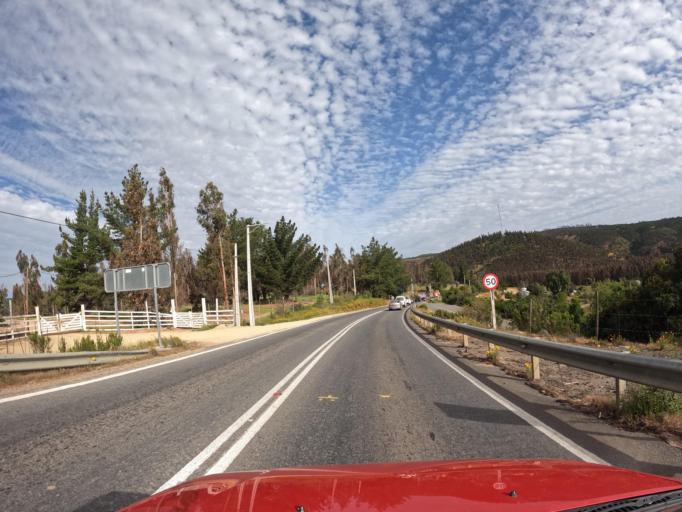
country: CL
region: O'Higgins
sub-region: Provincia de Colchagua
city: Santa Cruz
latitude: -34.2972
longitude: -71.8010
